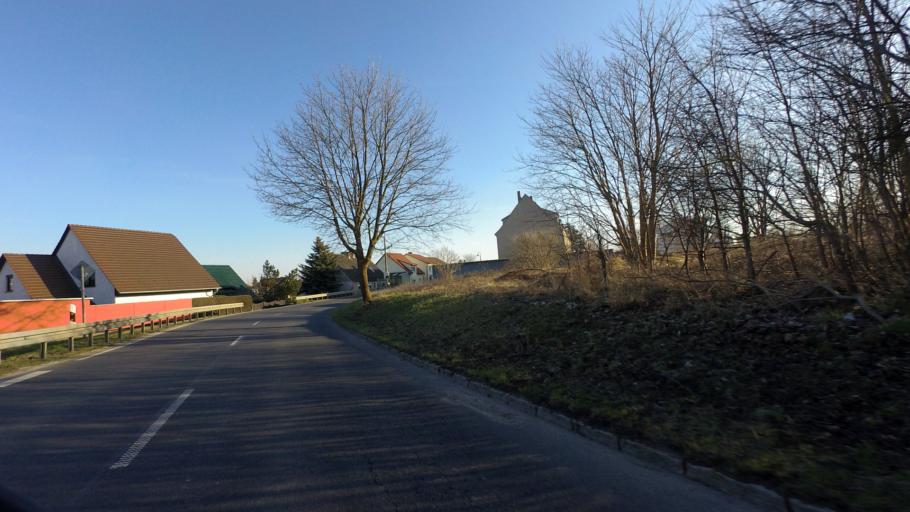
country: DE
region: Brandenburg
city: Britz
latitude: 52.9140
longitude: 13.8044
